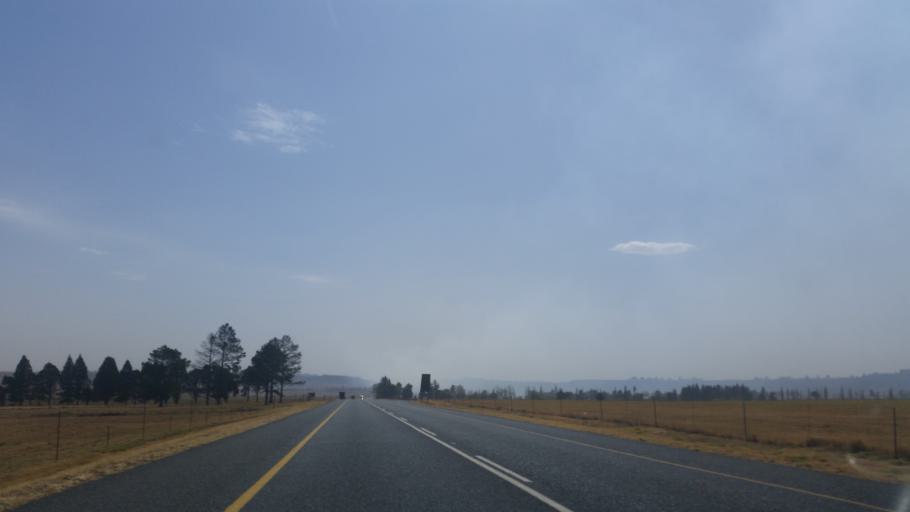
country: ZA
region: Orange Free State
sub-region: Thabo Mofutsanyana District Municipality
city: Bethlehem
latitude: -28.2838
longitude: 28.3961
